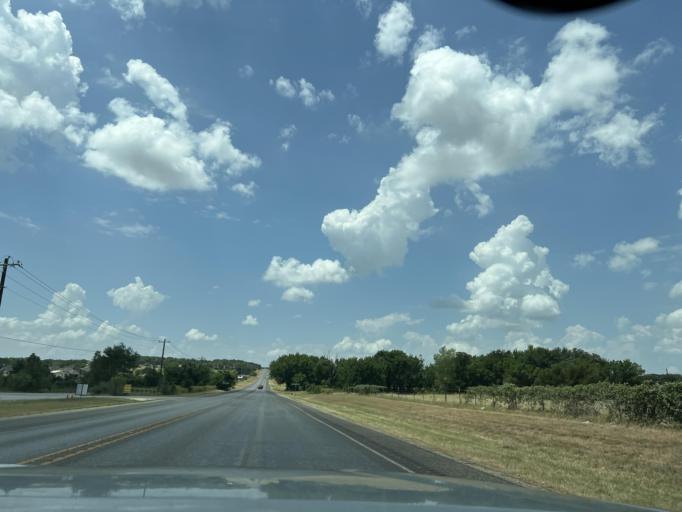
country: US
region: Texas
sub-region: Parker County
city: Springtown
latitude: 32.9427
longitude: -97.6943
